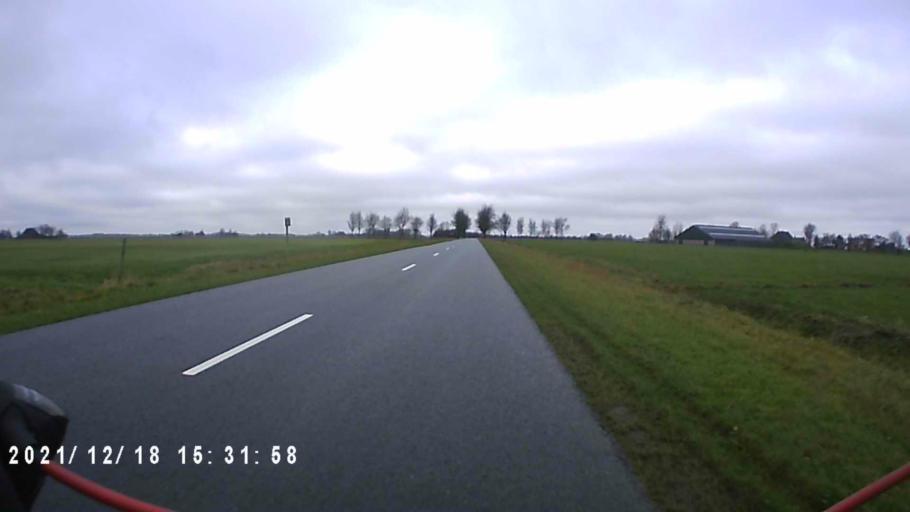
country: NL
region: Friesland
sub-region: Gemeente Dongeradeel
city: Anjum
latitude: 53.3407
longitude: 6.1357
